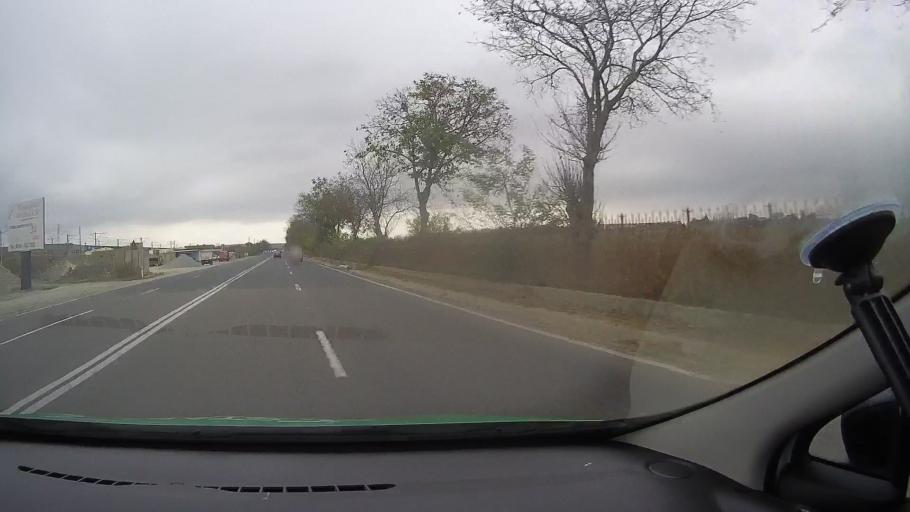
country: RO
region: Constanta
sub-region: Oras Murfatlar
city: Murfatlar
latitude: 44.1712
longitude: 28.4262
